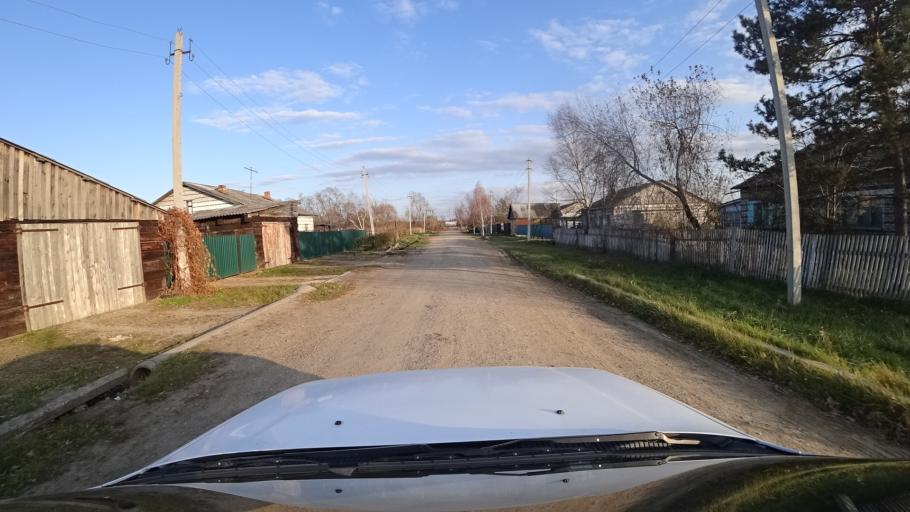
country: RU
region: Primorskiy
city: Lazo
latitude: 45.8272
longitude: 133.6152
